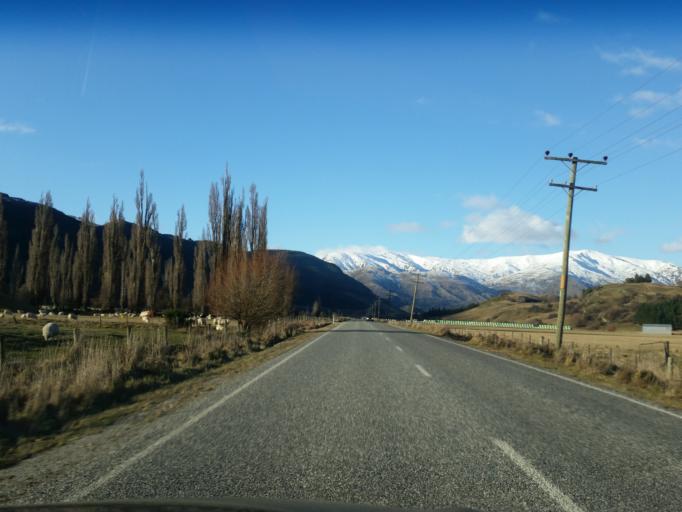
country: NZ
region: Otago
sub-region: Queenstown-Lakes District
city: Arrowtown
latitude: -44.9526
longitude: 168.7477
